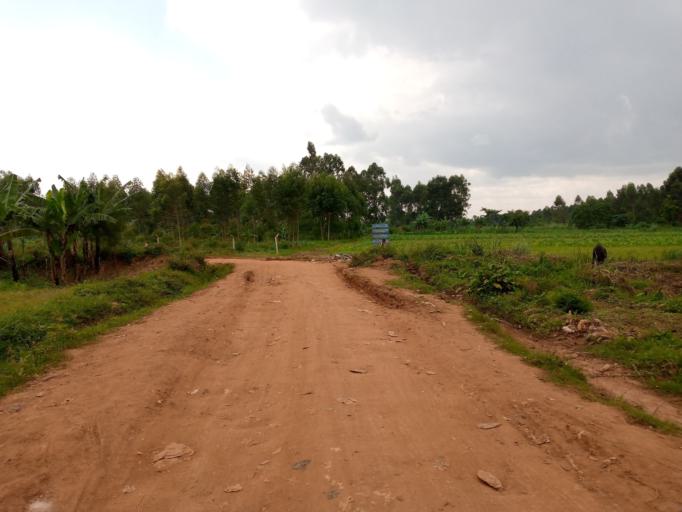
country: UG
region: Eastern Region
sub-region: Mbale District
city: Mbale
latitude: 1.0893
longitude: 34.1633
